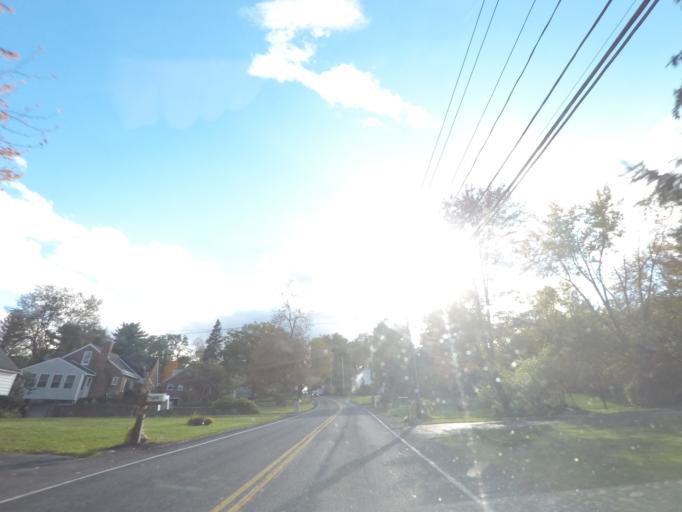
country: US
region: New York
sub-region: Schenectady County
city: Niskayuna
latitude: 42.7696
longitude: -73.8267
